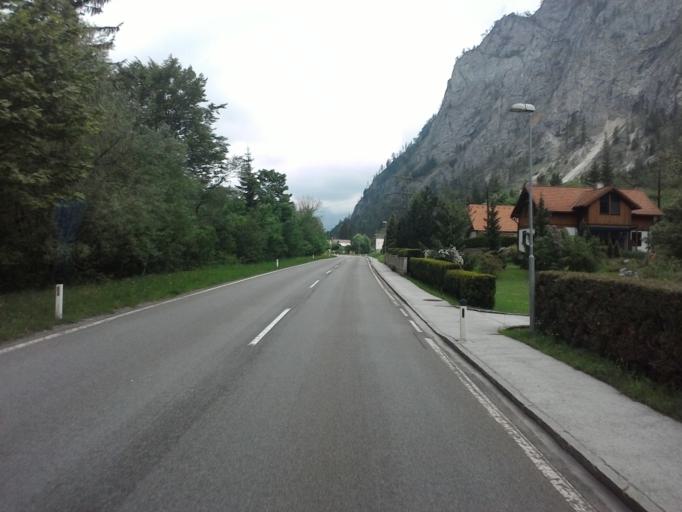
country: AT
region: Styria
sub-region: Politischer Bezirk Leoben
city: Hieflau
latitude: 47.6185
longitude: 14.7507
